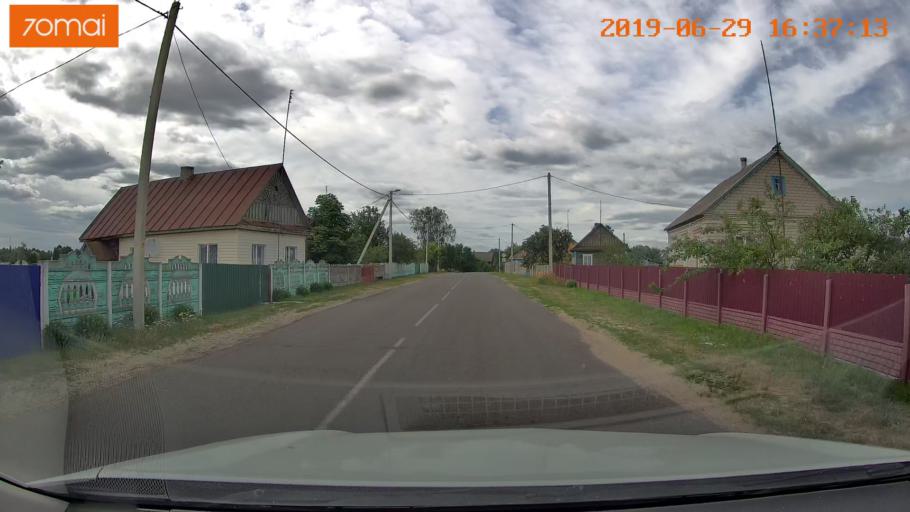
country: BY
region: Brest
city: Luninyets
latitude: 52.2259
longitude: 27.0226
